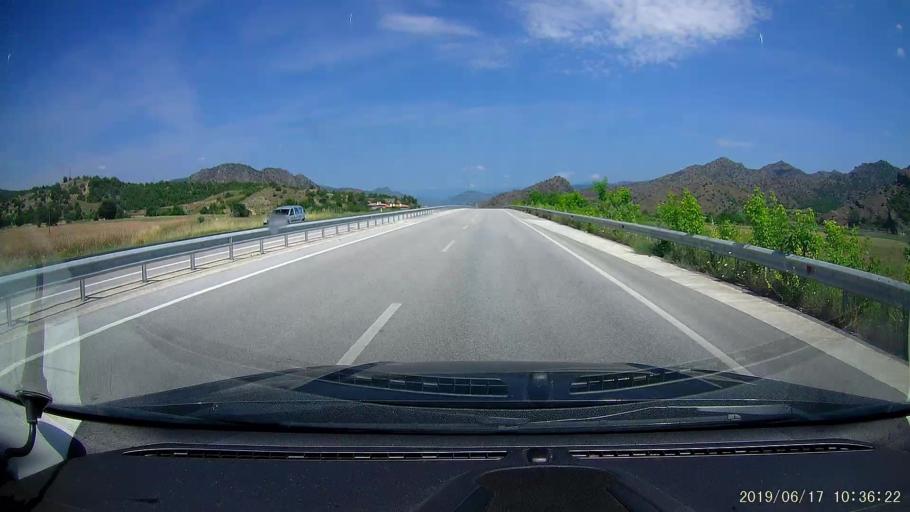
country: TR
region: Corum
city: Osmancik
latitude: 40.9781
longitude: 34.6829
